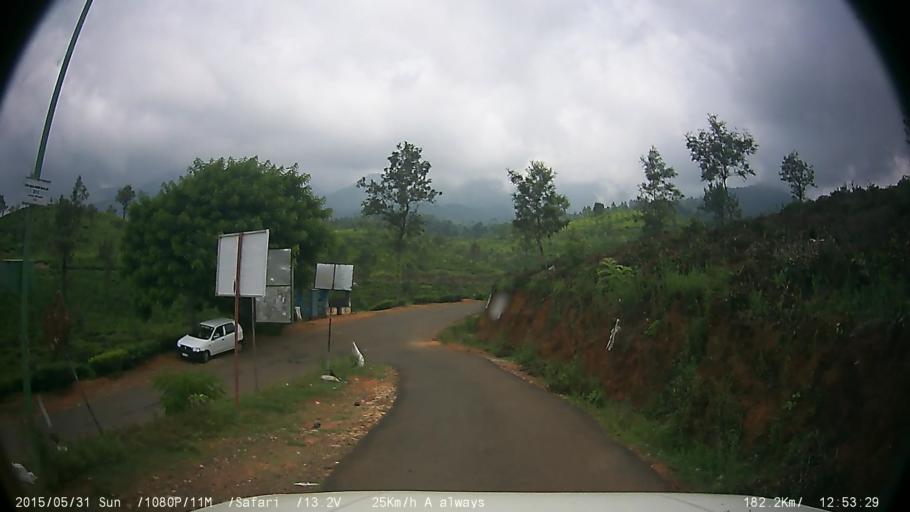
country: IN
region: Kerala
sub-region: Wayanad
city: Kalpetta
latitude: 11.5049
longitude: 76.1483
